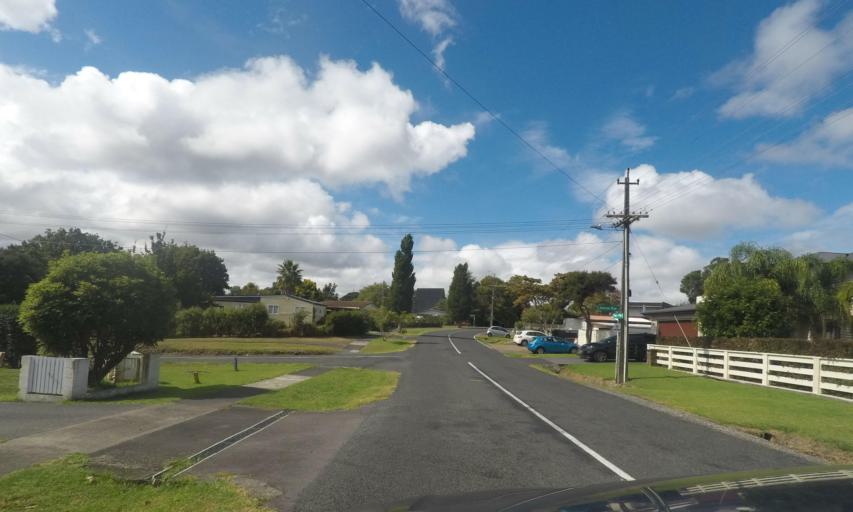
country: NZ
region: Auckland
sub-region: Auckland
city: Rosebank
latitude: -36.7808
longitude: 174.6547
